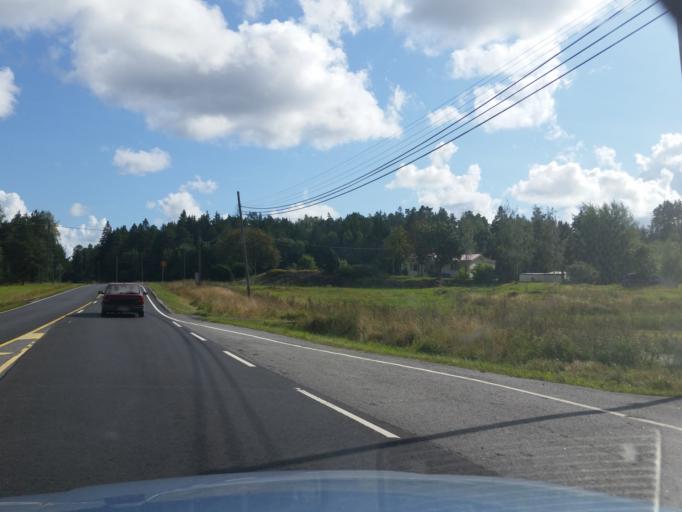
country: FI
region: Varsinais-Suomi
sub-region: Aboland-Turunmaa
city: Laensi-Turunmaa
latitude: 60.2585
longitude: 22.2285
